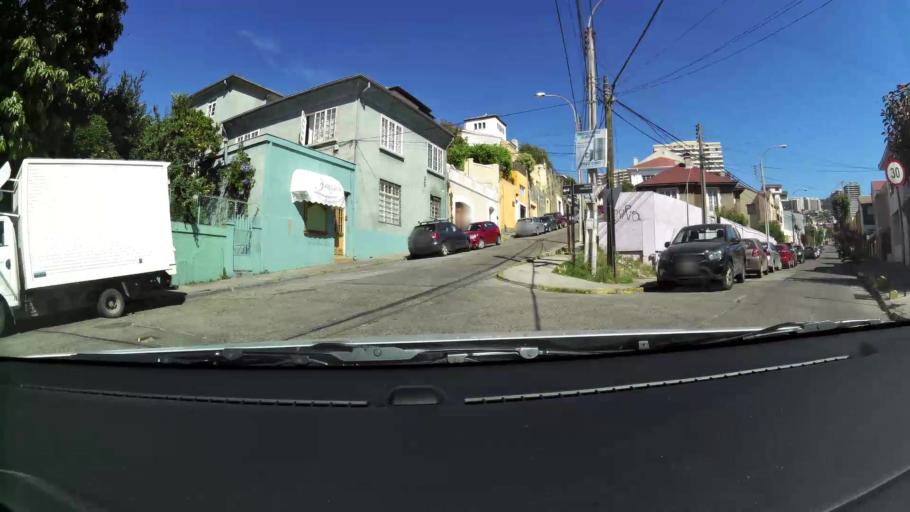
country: CL
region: Valparaiso
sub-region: Provincia de Valparaiso
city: Vina del Mar
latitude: -33.0286
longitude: -71.5747
